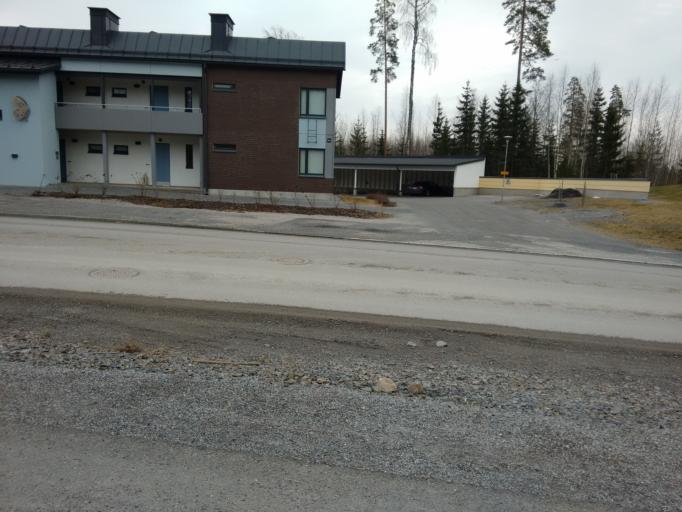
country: FI
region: Pirkanmaa
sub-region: Tampere
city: Tampere
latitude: 61.4316
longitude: 23.8273
